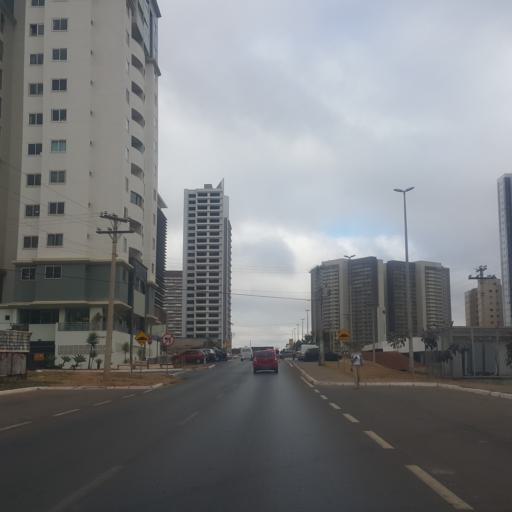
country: BR
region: Federal District
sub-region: Brasilia
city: Brasilia
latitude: -15.8365
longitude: -48.0375
